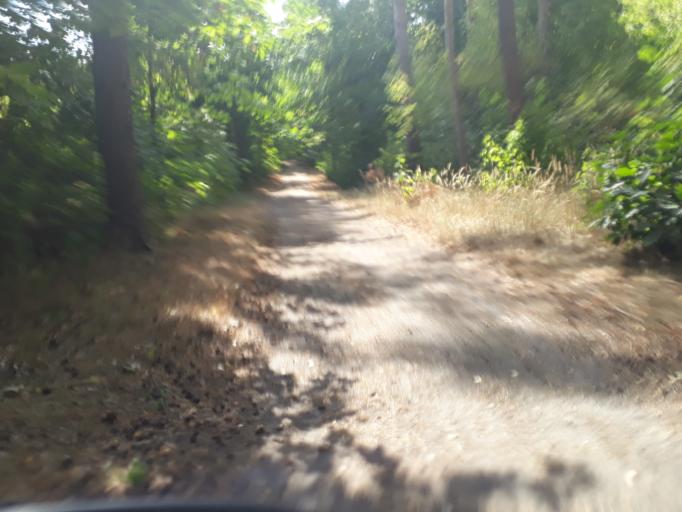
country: DE
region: Berlin
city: Grunewald
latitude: 52.4889
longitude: 13.2486
